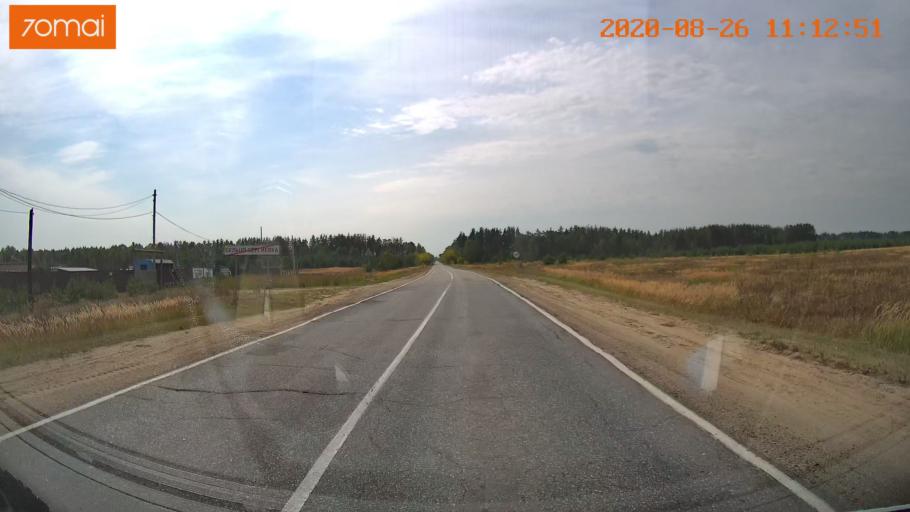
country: RU
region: Rjazan
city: Izhevskoye
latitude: 54.4659
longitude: 41.1240
